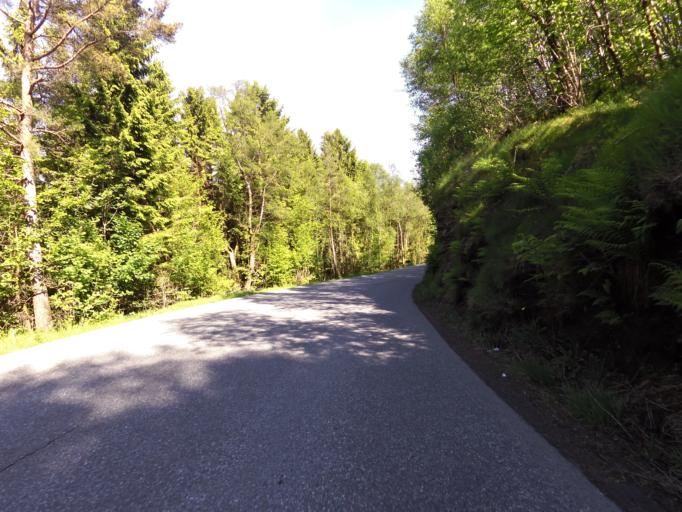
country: NO
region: Hordaland
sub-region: Stord
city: Leirvik
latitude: 59.7878
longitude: 5.4759
